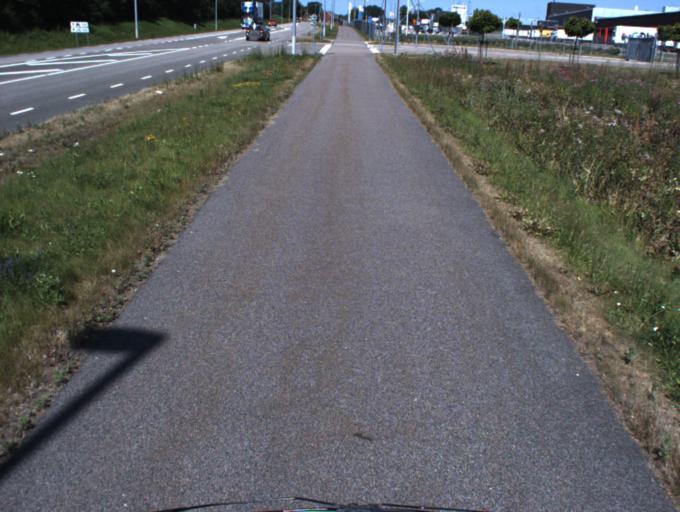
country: SE
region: Skane
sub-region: Helsingborg
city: Barslov
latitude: 56.0354
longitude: 12.7808
